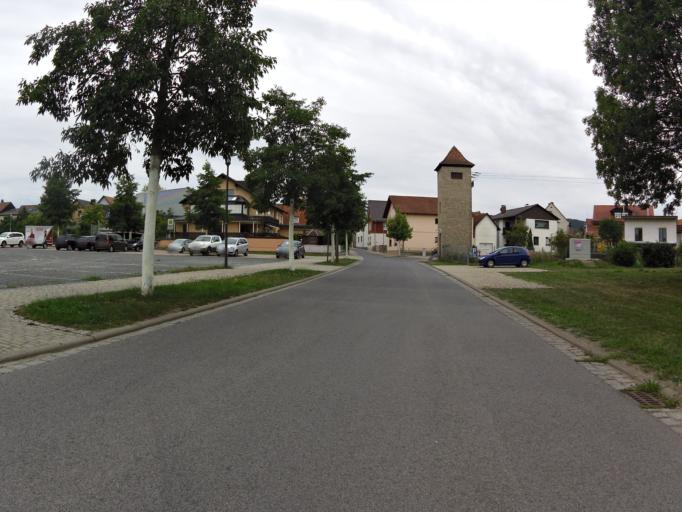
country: DE
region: Bavaria
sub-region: Regierungsbezirk Unterfranken
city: Sand
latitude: 49.9903
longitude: 10.5873
